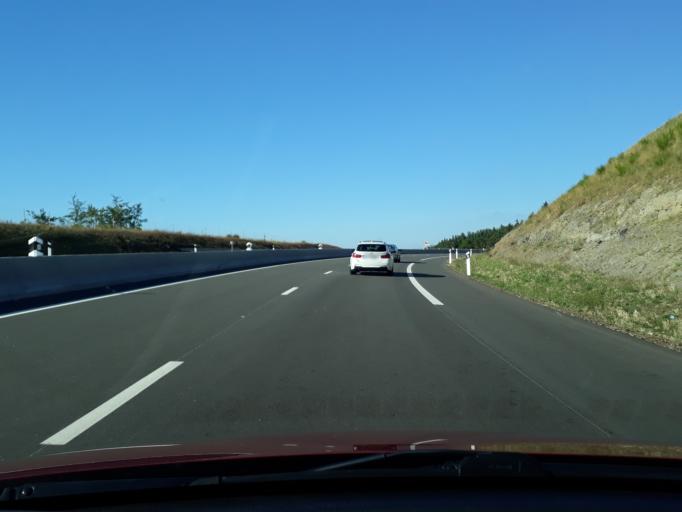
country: FR
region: Auvergne
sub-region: Departement de la Haute-Loire
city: Cussac-sur-Loire
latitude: 45.0098
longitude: 3.8835
